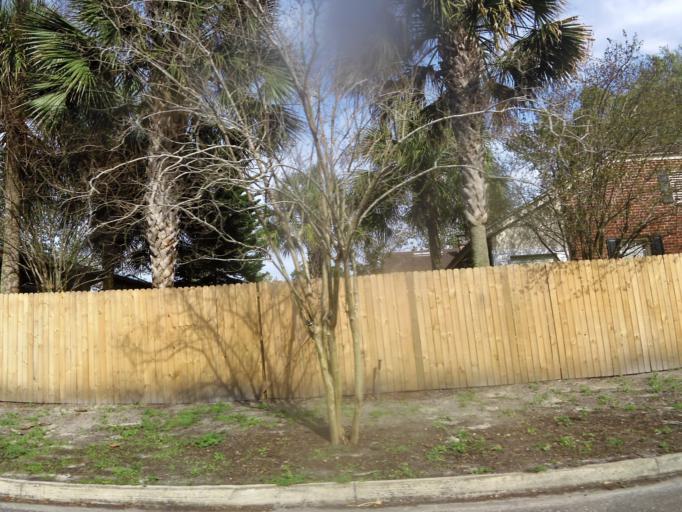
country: US
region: Florida
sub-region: Duval County
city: Jacksonville
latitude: 30.3140
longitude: -81.7244
